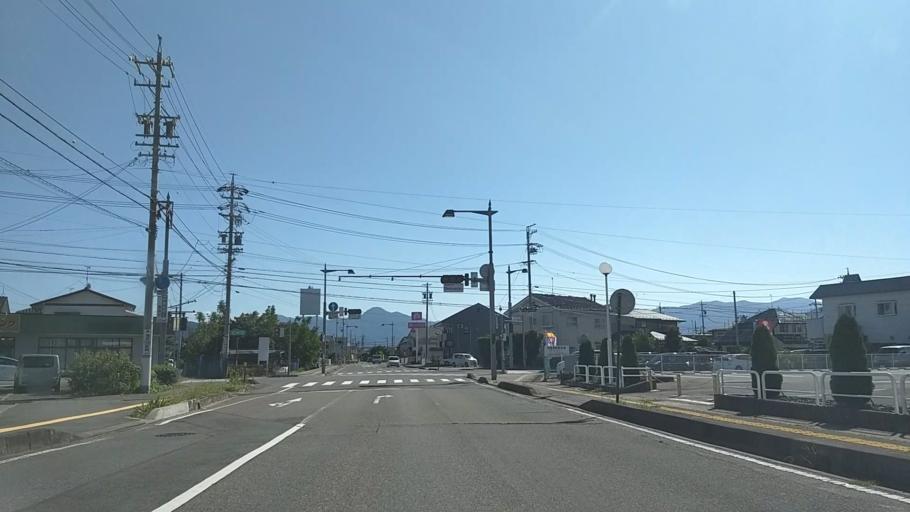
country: JP
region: Nagano
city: Nagano-shi
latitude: 36.5799
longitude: 138.1358
